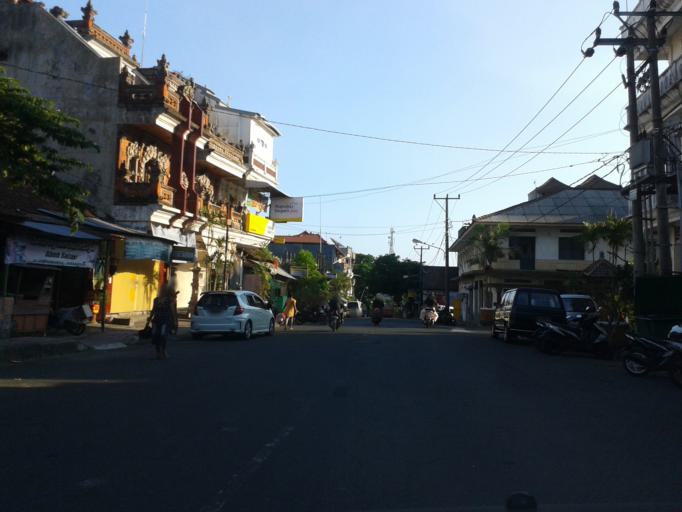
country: ID
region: Bali
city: Semarapura
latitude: -8.5358
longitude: 115.4059
